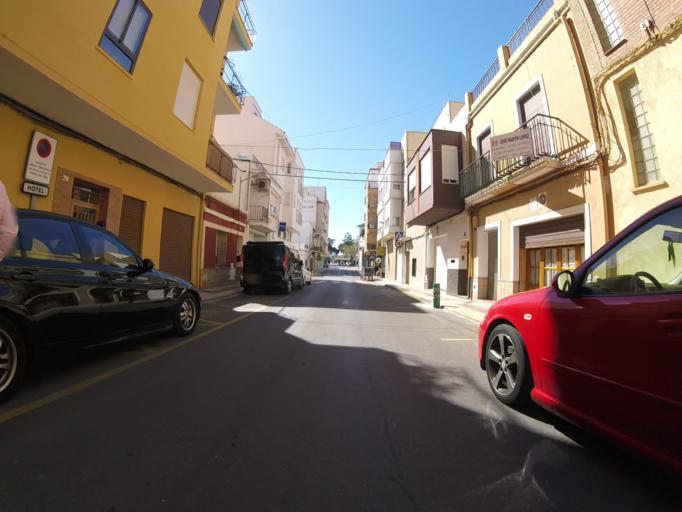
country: ES
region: Valencia
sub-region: Provincia de Castello
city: Benicassim
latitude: 40.0576
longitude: 0.0676
